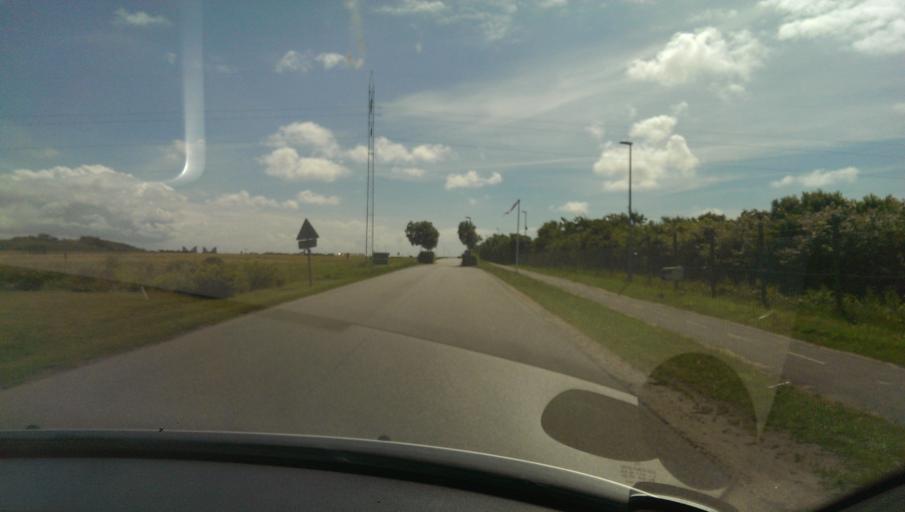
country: DK
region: Central Jutland
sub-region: Ringkobing-Skjern Kommune
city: Ringkobing
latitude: 56.1191
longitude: 8.1770
